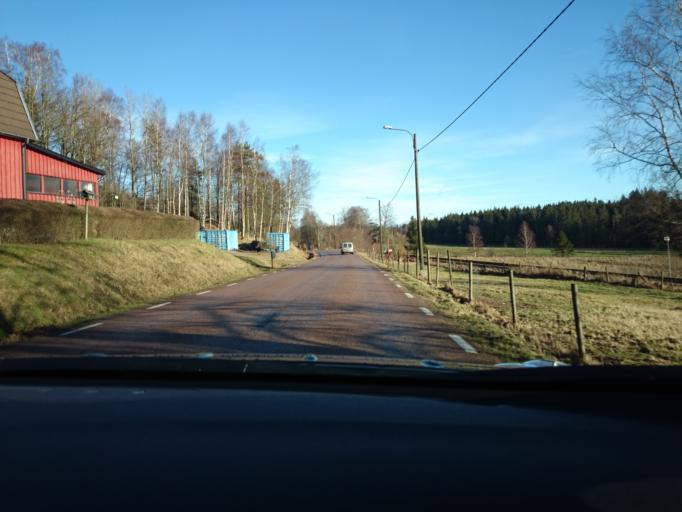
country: SE
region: Halland
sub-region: Hylte Kommun
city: Hyltebruk
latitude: 57.0706
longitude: 13.2461
